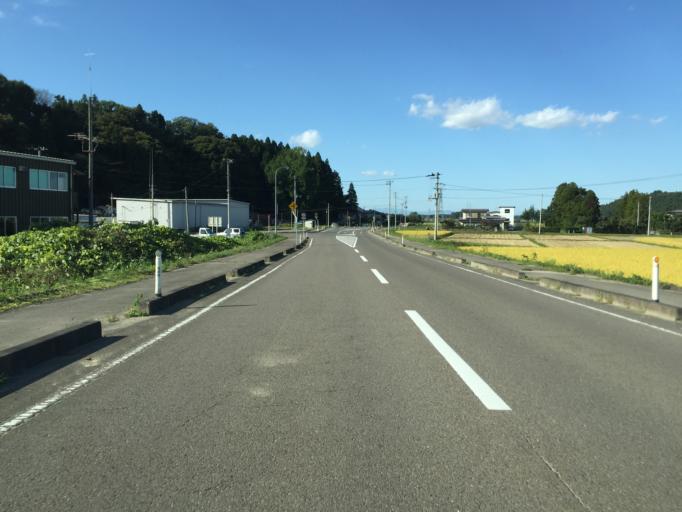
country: JP
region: Miyagi
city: Marumori
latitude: 37.8969
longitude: 140.7698
